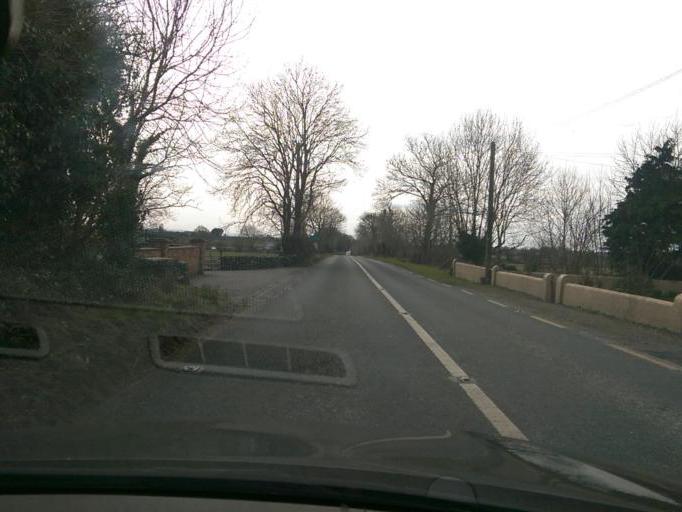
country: IE
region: Connaught
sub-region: County Galway
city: Claregalway
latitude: 53.3852
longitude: -8.8498
